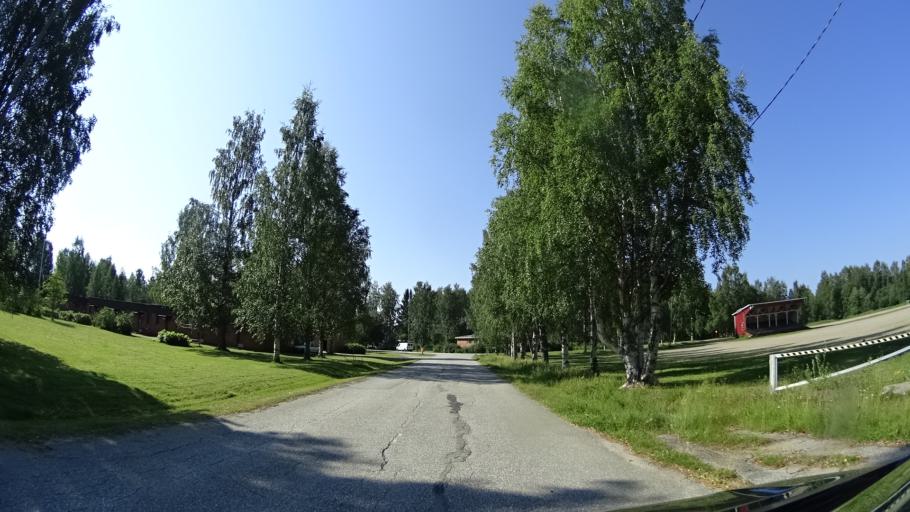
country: FI
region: North Karelia
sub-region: Joensuu
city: Juuka
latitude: 63.2372
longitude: 29.2454
